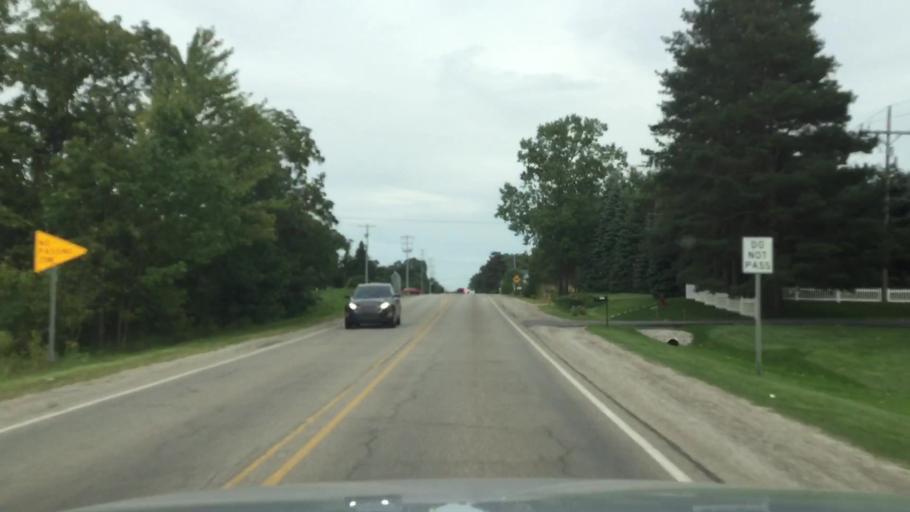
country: US
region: Michigan
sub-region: Genesee County
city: Grand Blanc
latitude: 42.8866
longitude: -83.6437
